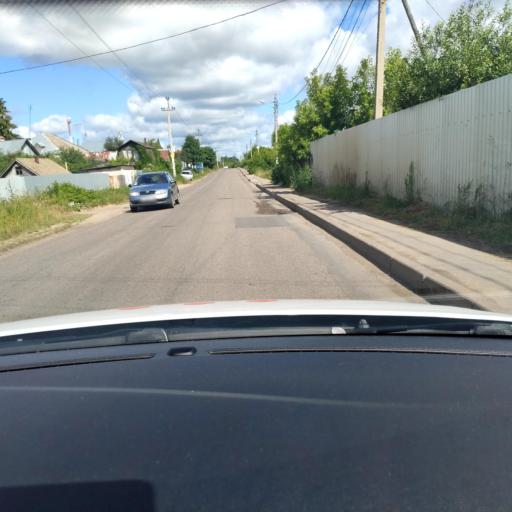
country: RU
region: Tatarstan
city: Vysokaya Gora
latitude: 55.8615
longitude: 49.2392
